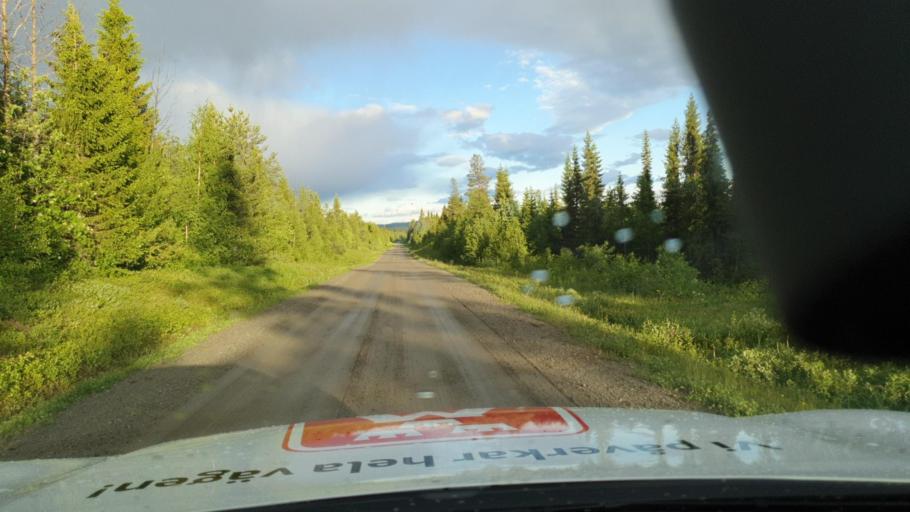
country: SE
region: Vaesterbotten
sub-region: Storumans Kommun
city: Storuman
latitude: 64.7593
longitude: 17.0719
